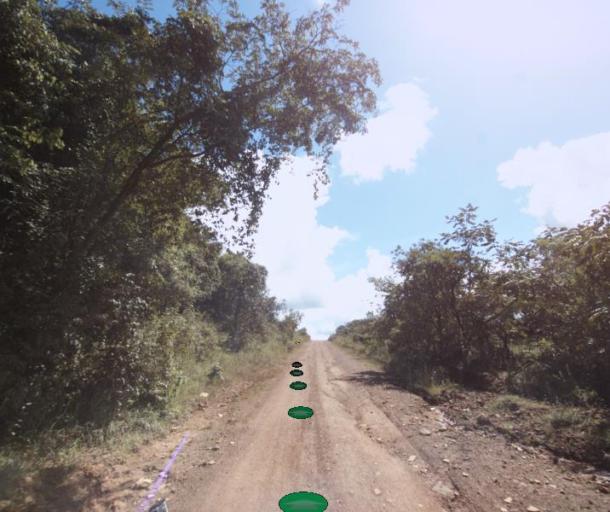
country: BR
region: Goias
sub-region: Pirenopolis
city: Pirenopolis
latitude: -15.7805
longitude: -48.8393
